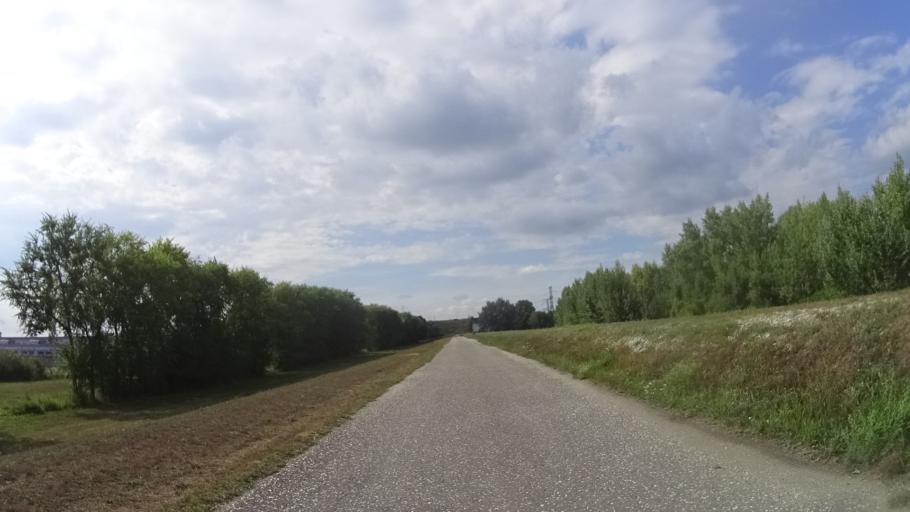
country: SK
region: Trnavsky
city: Gabcikovo
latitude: 47.8794
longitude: 17.5475
